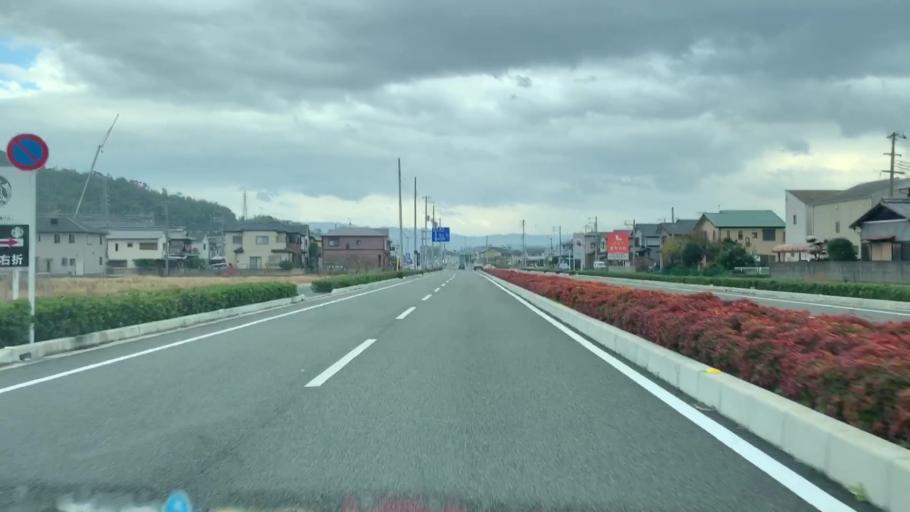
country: JP
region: Wakayama
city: Wakayama-shi
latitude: 34.2186
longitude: 135.2074
